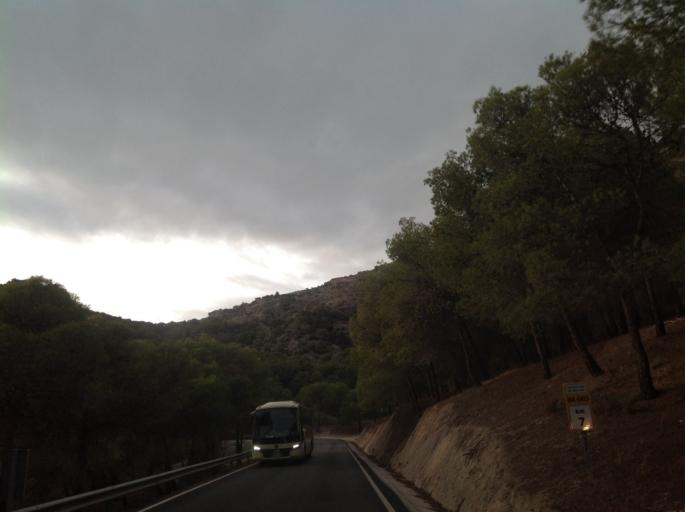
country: ES
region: Andalusia
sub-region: Provincia de Malaga
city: Ardales
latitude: 36.9125
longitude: -4.7953
